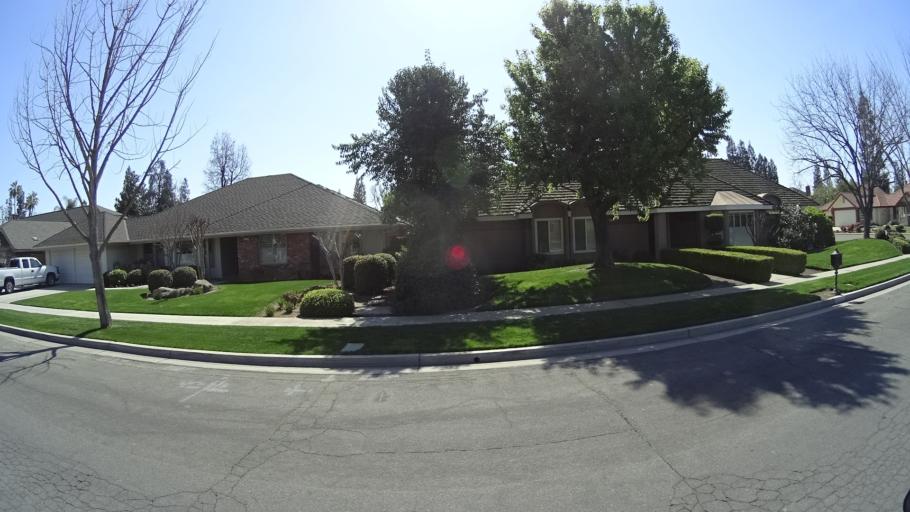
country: US
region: California
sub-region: Fresno County
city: Fresno
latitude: 36.8403
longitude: -119.8216
